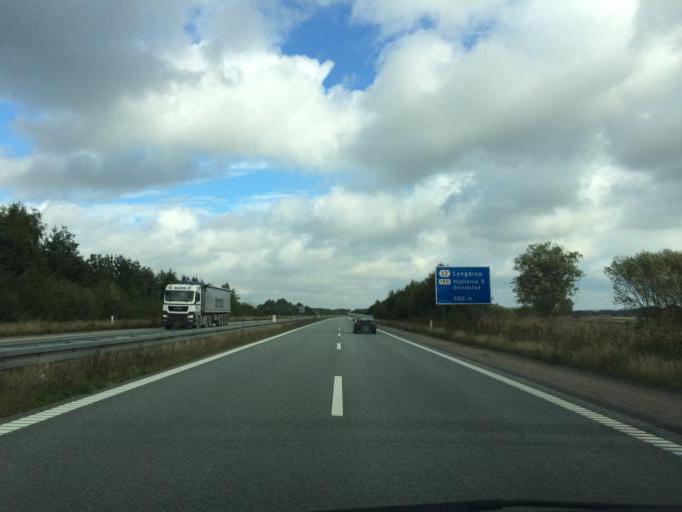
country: DK
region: North Denmark
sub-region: Alborg Kommune
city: Vodskov
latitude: 57.1277
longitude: 10.0753
